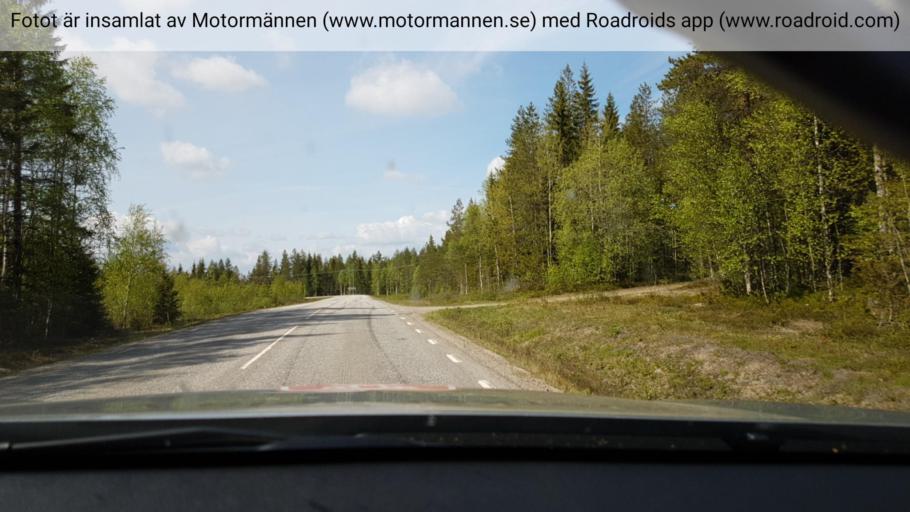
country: SE
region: Vaesterbotten
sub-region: Vannas Kommun
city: Vannasby
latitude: 63.8513
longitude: 19.9578
